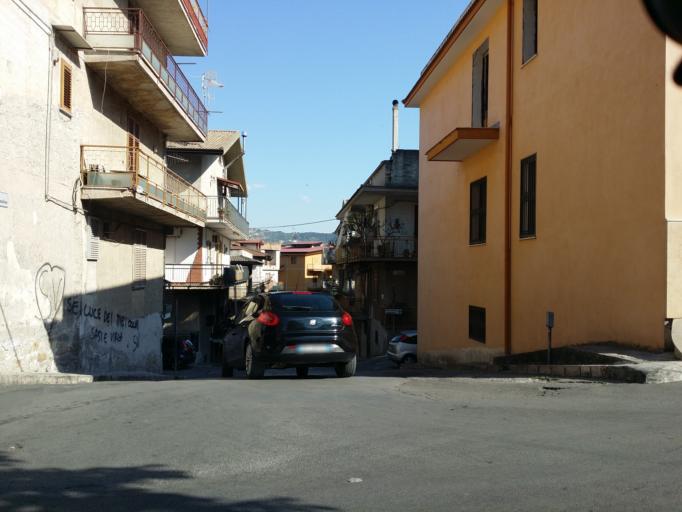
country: IT
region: Sicily
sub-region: Palermo
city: Misilmeri
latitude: 38.0310
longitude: 13.4461
